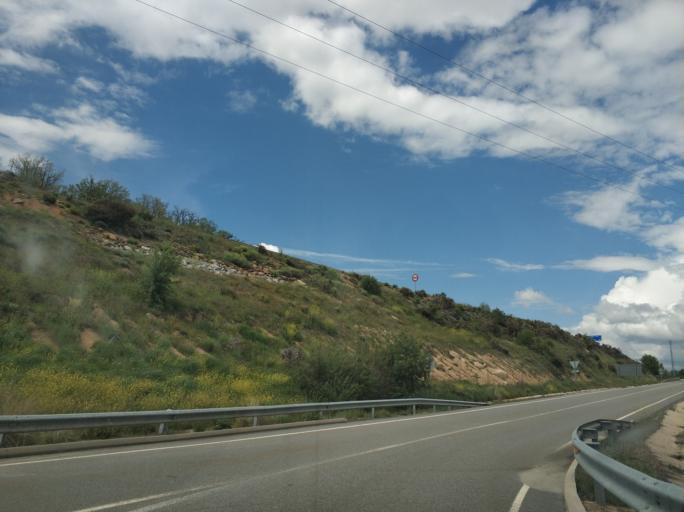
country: ES
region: Castille and Leon
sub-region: Provincia de Salamanca
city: Sorihuela
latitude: 40.4406
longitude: -5.6889
